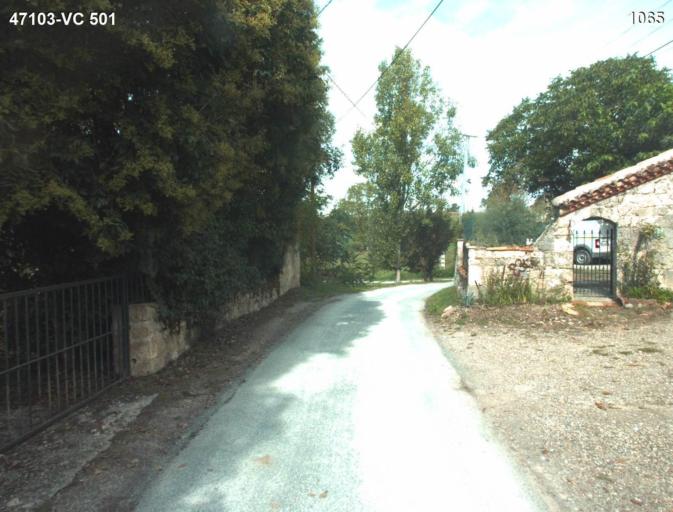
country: FR
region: Aquitaine
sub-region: Departement du Lot-et-Garonne
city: Nerac
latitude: 44.0965
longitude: 0.3408
